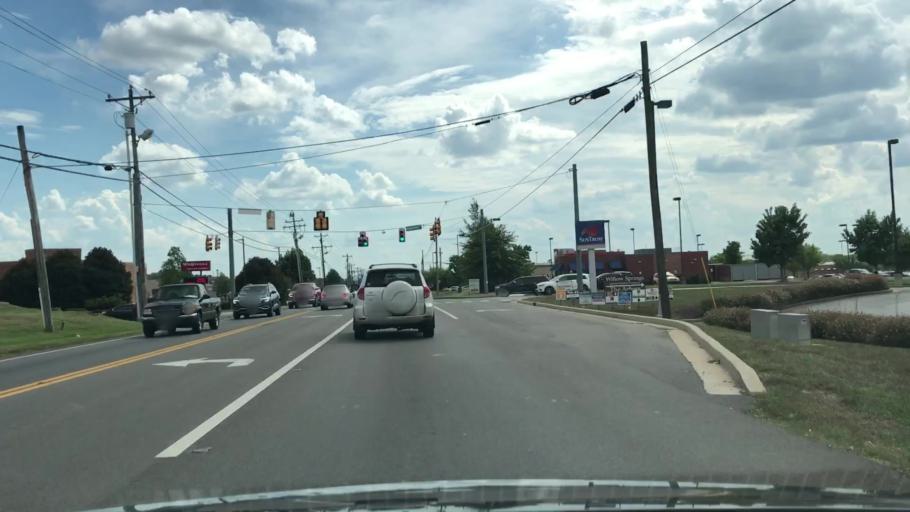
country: US
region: Tennessee
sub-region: Williamson County
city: Thompson's Station
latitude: 35.7759
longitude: -86.9158
